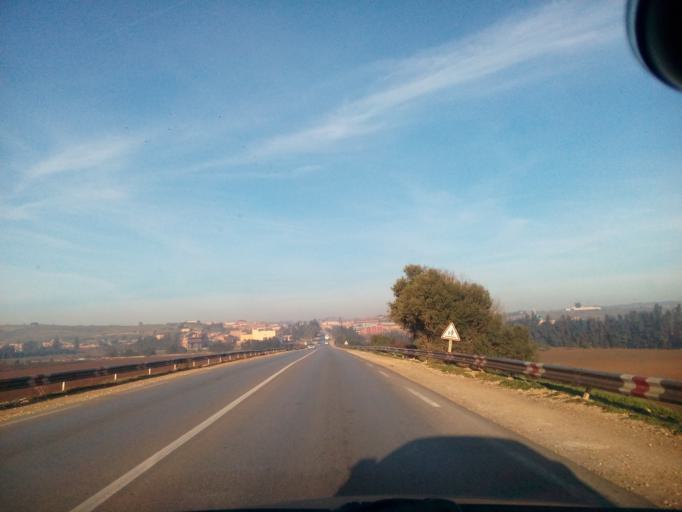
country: DZ
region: Relizane
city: Relizane
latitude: 35.7164
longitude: 0.3342
